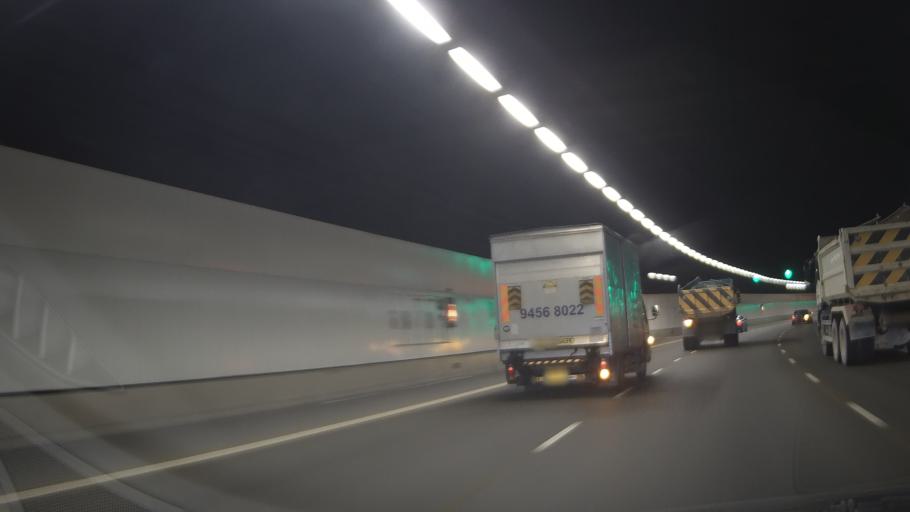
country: SG
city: Singapore
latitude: 1.2852
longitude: 103.8664
